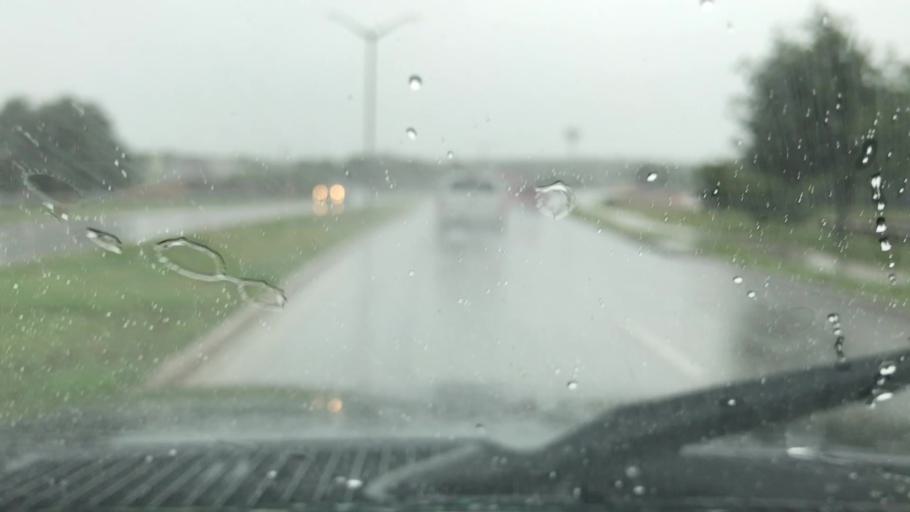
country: US
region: Texas
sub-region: Williamson County
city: Cedar Park
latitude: 30.5294
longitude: -97.8570
